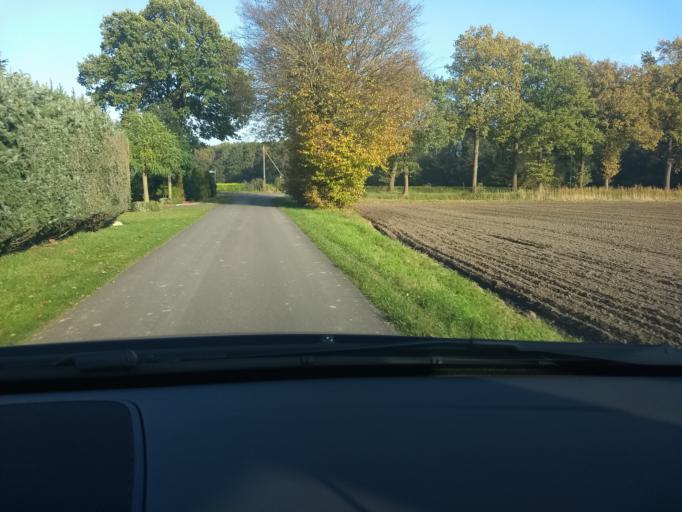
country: DE
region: North Rhine-Westphalia
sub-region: Regierungsbezirk Munster
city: Borken
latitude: 51.8831
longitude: 6.8507
